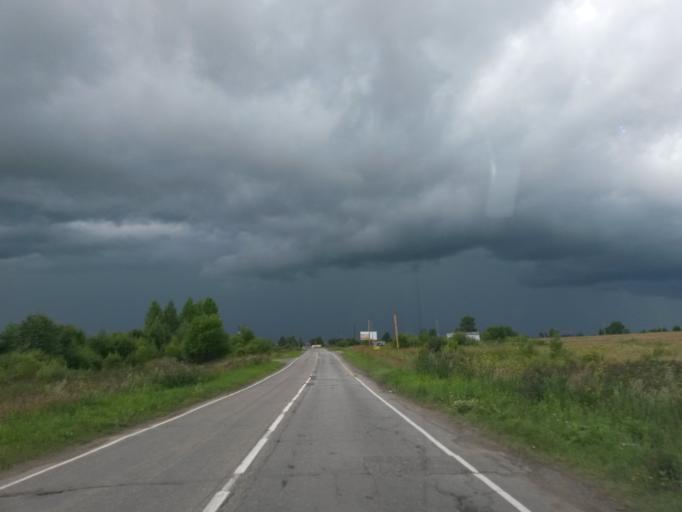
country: RU
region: Jaroslavl
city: Tutayev
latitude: 57.8778
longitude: 39.5695
